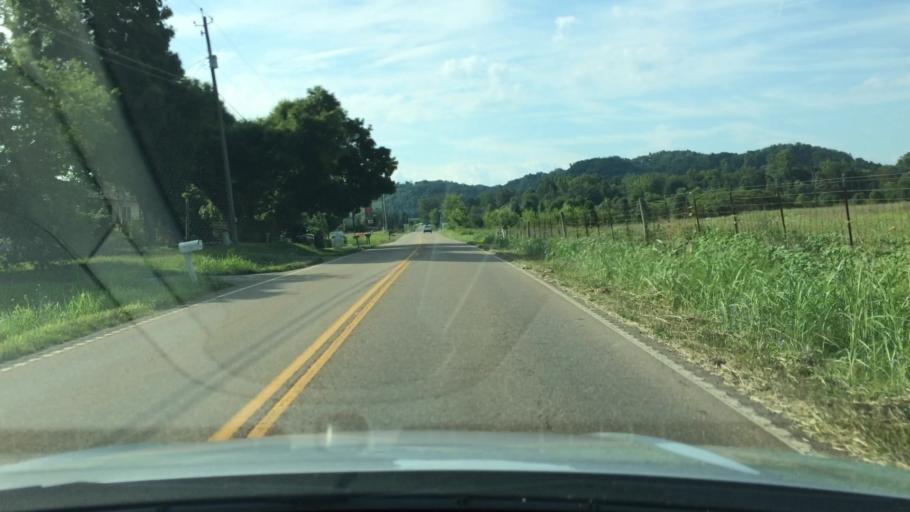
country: US
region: Tennessee
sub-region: Sevier County
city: Seymour
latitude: 35.9229
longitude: -83.6479
